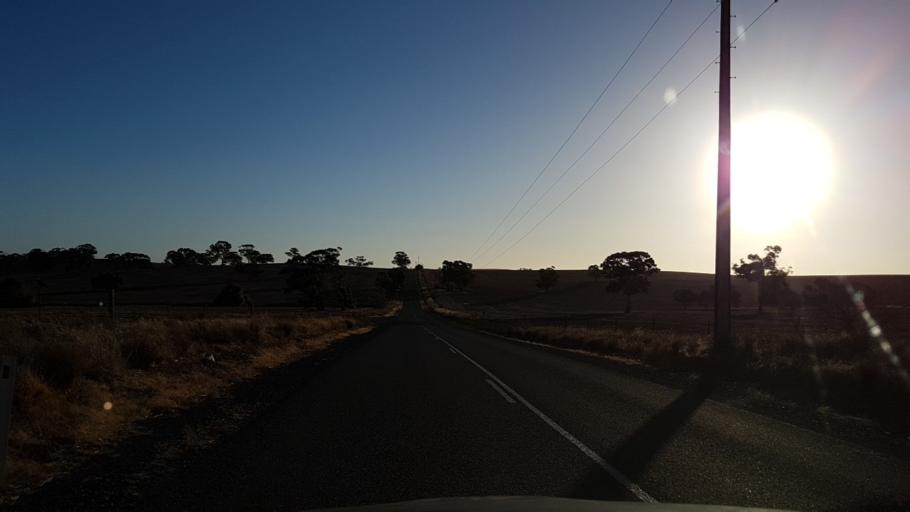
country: AU
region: South Australia
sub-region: Clare and Gilbert Valleys
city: Clare
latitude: -34.0176
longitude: 138.7170
